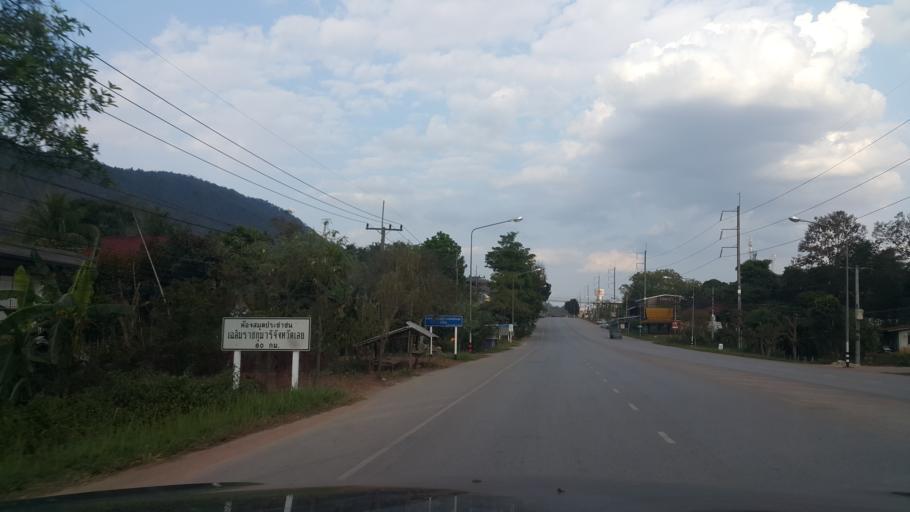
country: TH
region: Loei
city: Dan Sai
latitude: 17.2808
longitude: 101.1709
